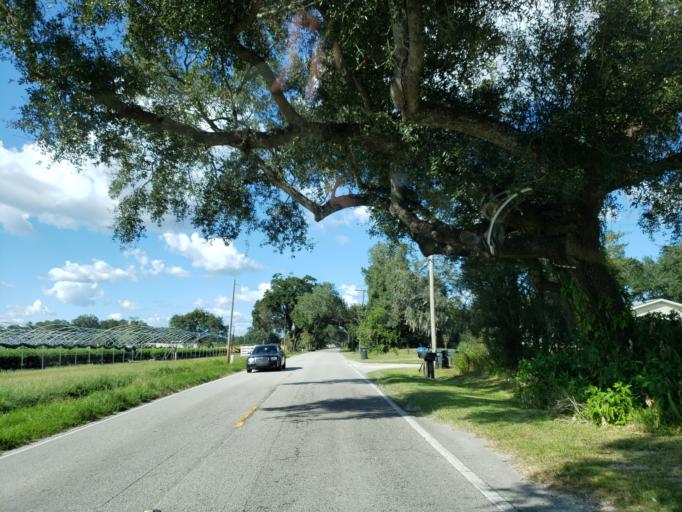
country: US
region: Florida
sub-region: Hillsborough County
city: Dover
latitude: 27.9882
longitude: -82.1870
